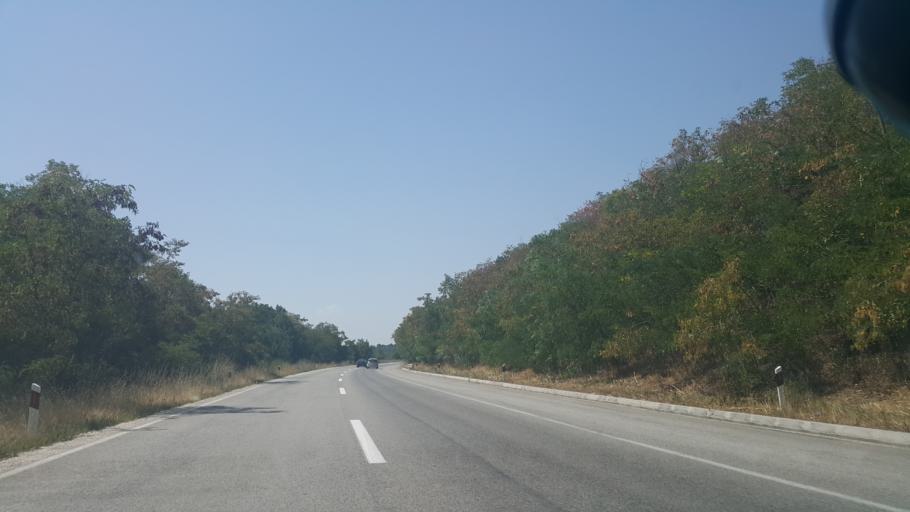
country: MK
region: Veles
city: Ivankovci
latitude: 41.8373
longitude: 21.7265
